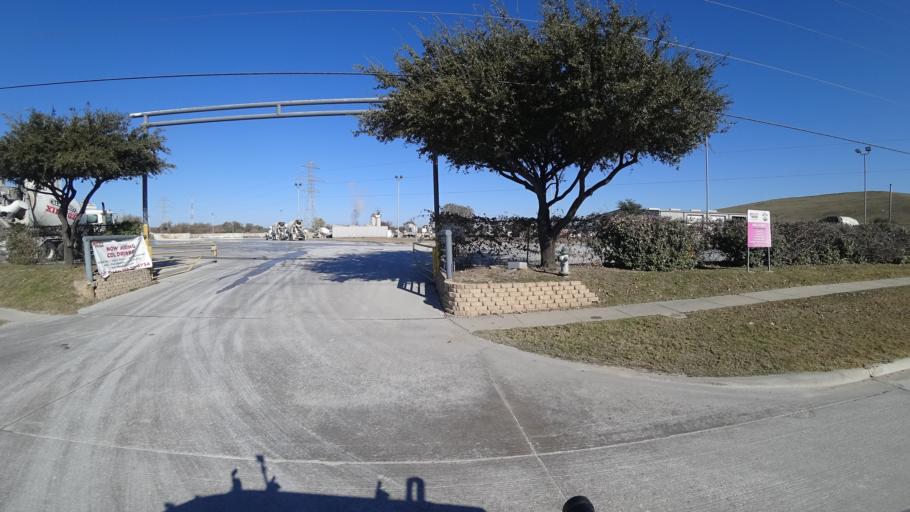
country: US
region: Texas
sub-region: Denton County
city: Lewisville
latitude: 33.0494
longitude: -96.9822
